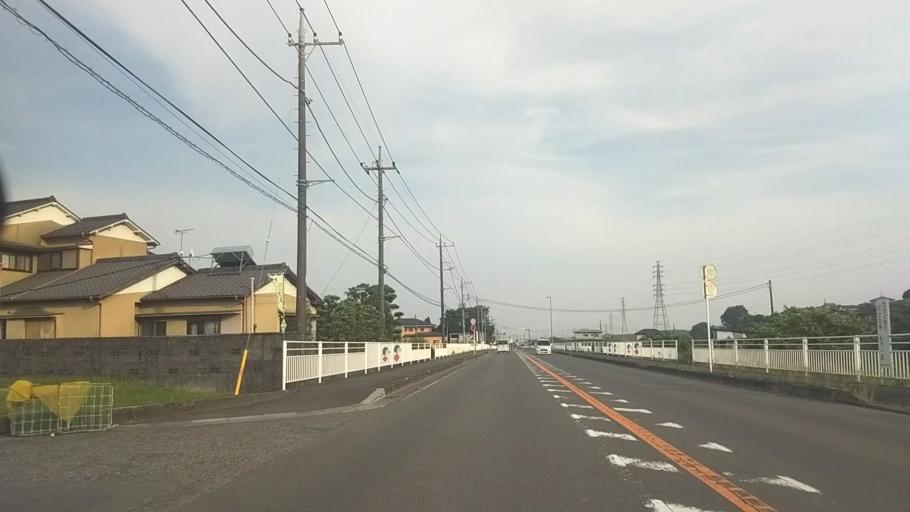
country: JP
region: Kanagawa
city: Odawara
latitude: 35.3416
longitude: 139.1019
